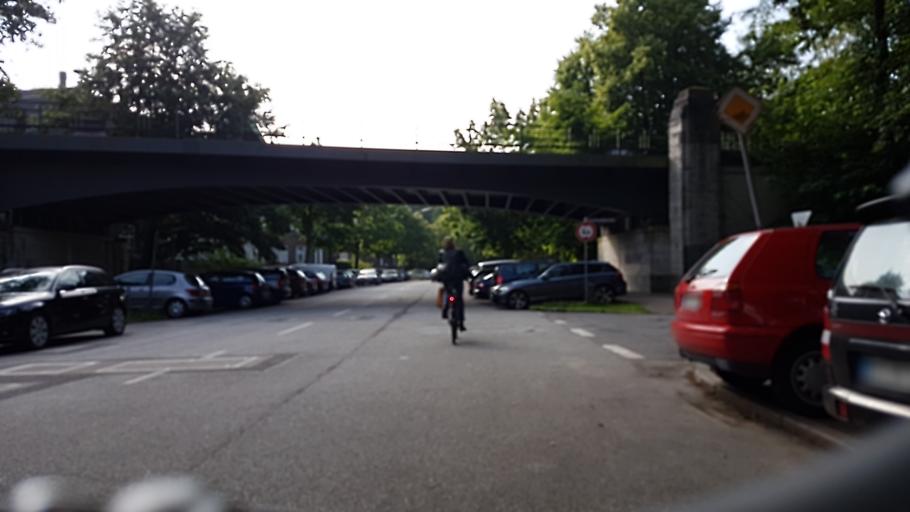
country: DE
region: Hamburg
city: Winterhude
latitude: 53.5914
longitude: 9.9943
